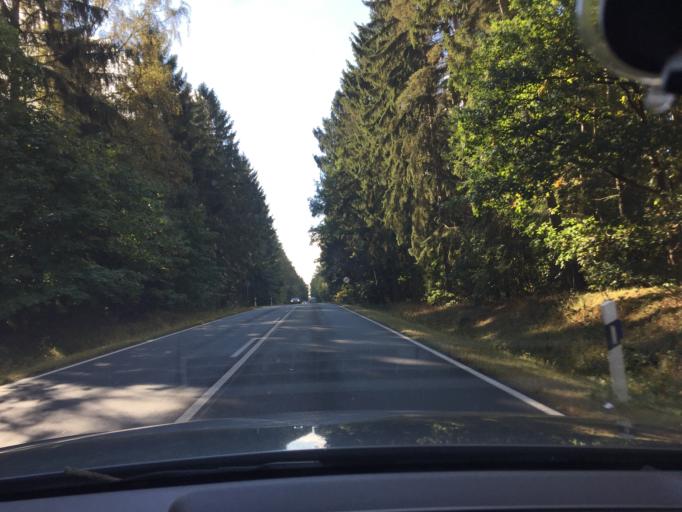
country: DE
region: Mecklenburg-Vorpommern
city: Krakow am See
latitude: 53.6325
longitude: 12.2551
